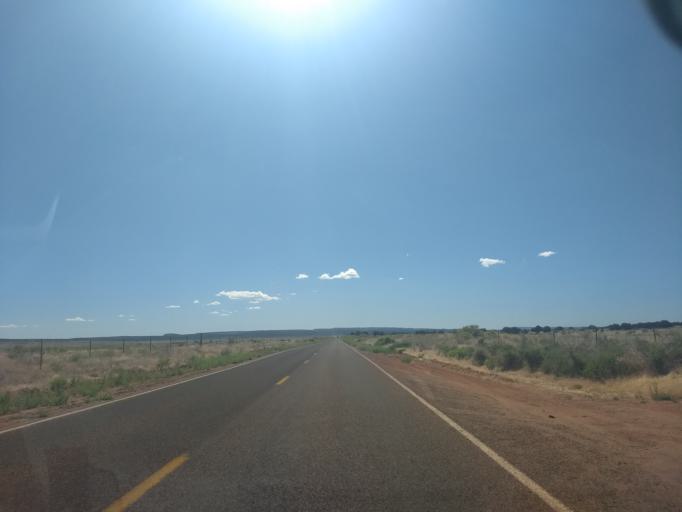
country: US
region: Arizona
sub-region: Mohave County
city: Colorado City
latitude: 36.9469
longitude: -112.9393
